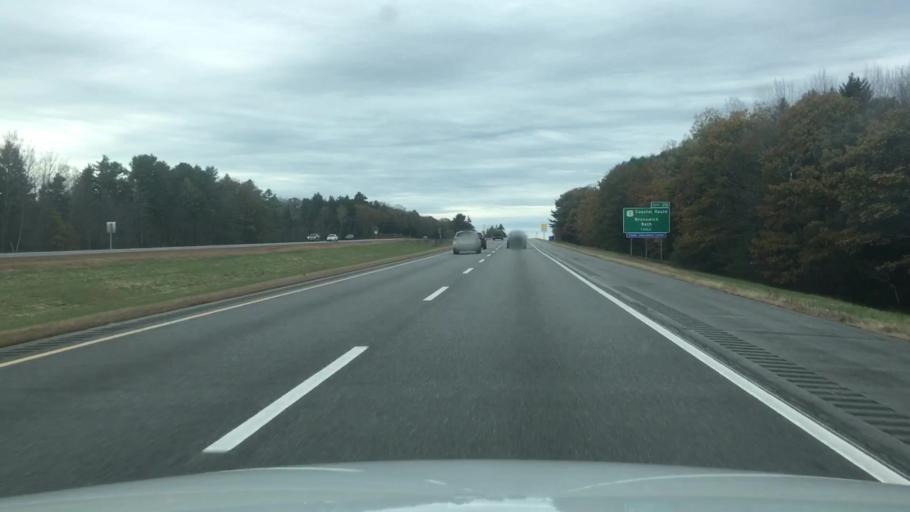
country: US
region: Maine
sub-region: Sagadahoc County
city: Topsham
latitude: 43.9243
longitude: -70.0060
